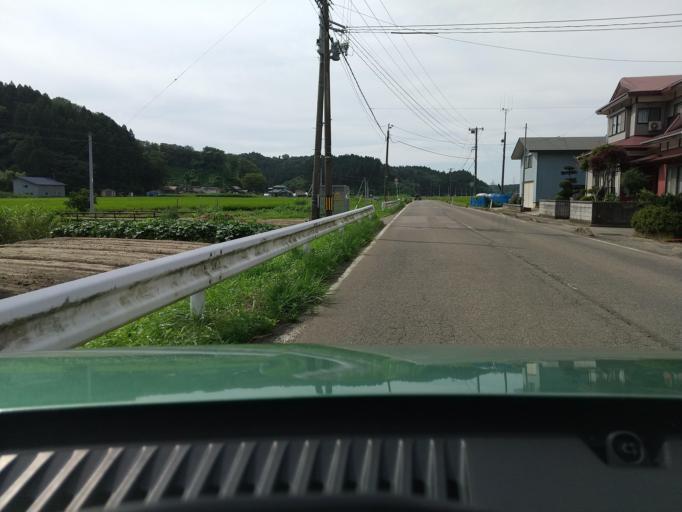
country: JP
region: Akita
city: Akita
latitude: 39.7829
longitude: 140.1287
